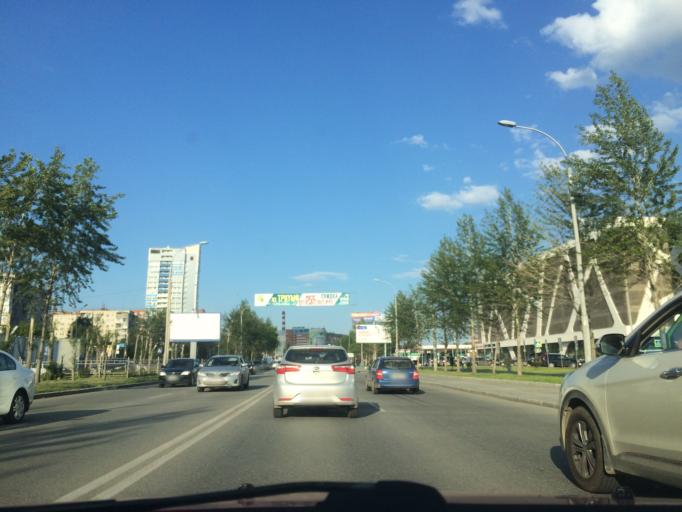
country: RU
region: Sverdlovsk
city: Yekaterinburg
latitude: 56.8176
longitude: 60.6308
